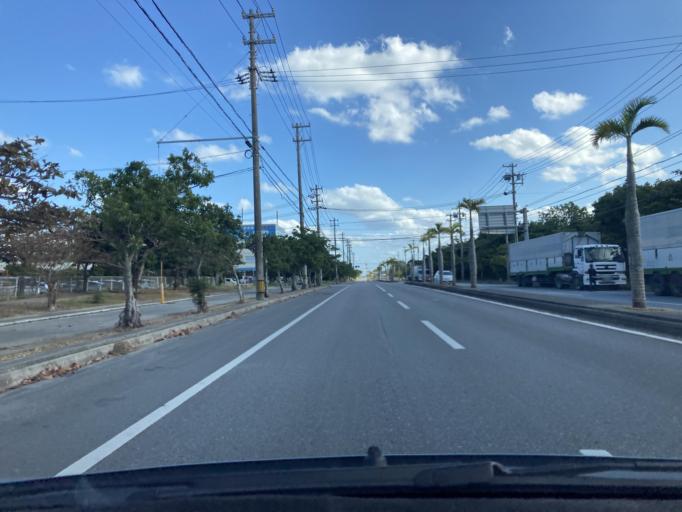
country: JP
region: Okinawa
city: Katsuren-haebaru
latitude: 26.3337
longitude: 127.8515
